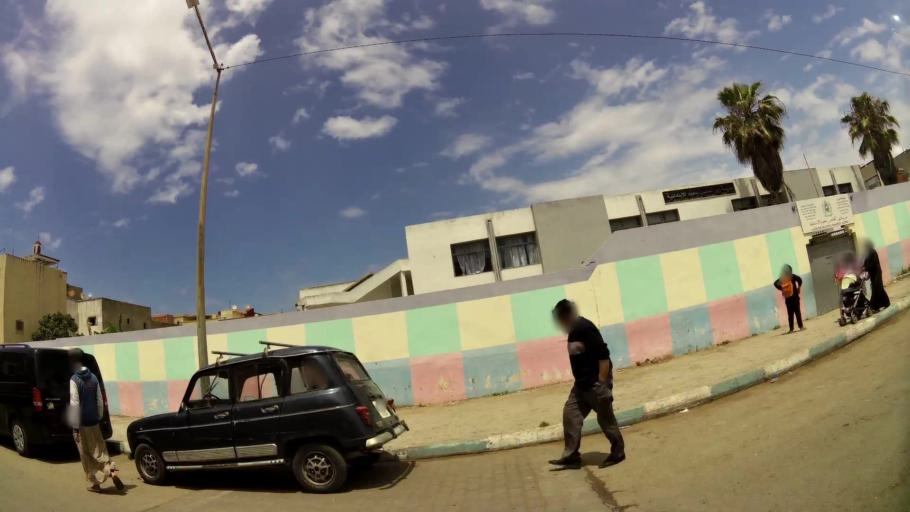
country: MA
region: Rabat-Sale-Zemmour-Zaer
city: Sale
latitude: 34.0533
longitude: -6.8176
